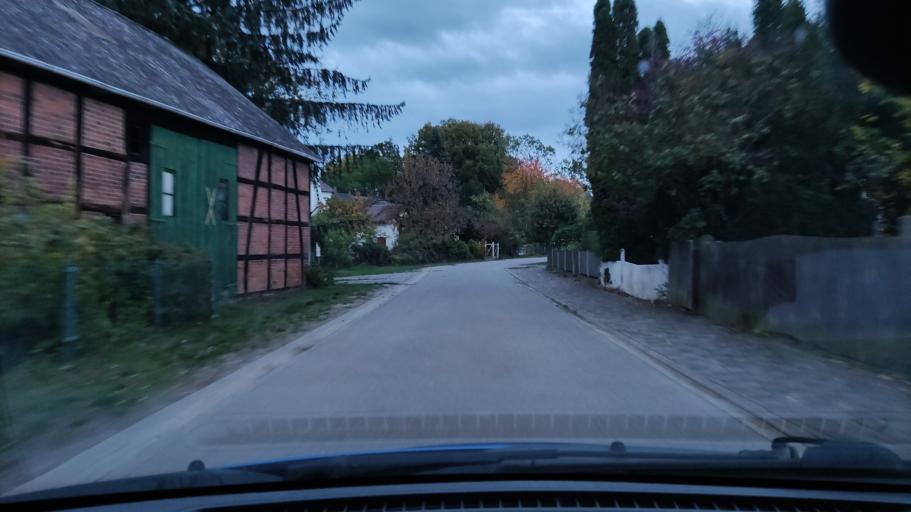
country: DE
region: Lower Saxony
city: Gorleben
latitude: 53.0701
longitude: 11.4041
